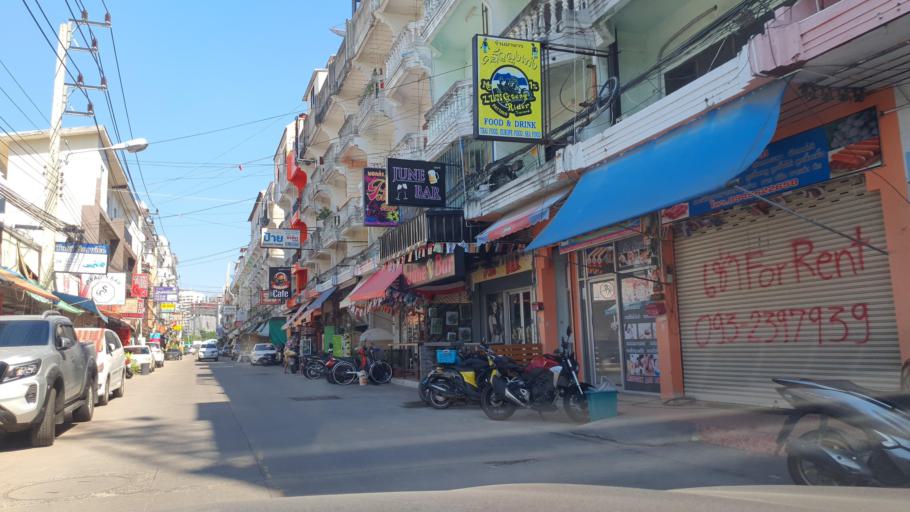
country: TH
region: Chon Buri
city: Phatthaya
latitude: 12.8868
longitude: 100.8799
